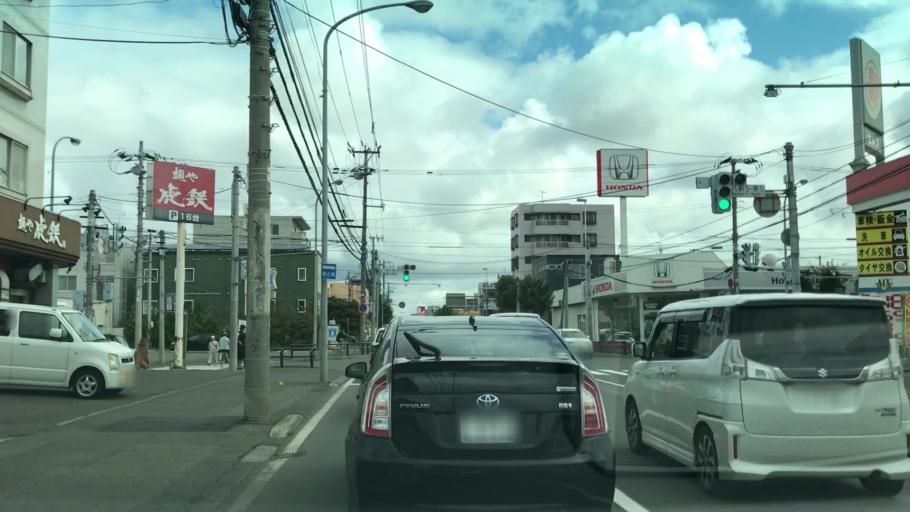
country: JP
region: Hokkaido
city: Sapporo
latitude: 43.0826
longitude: 141.3219
